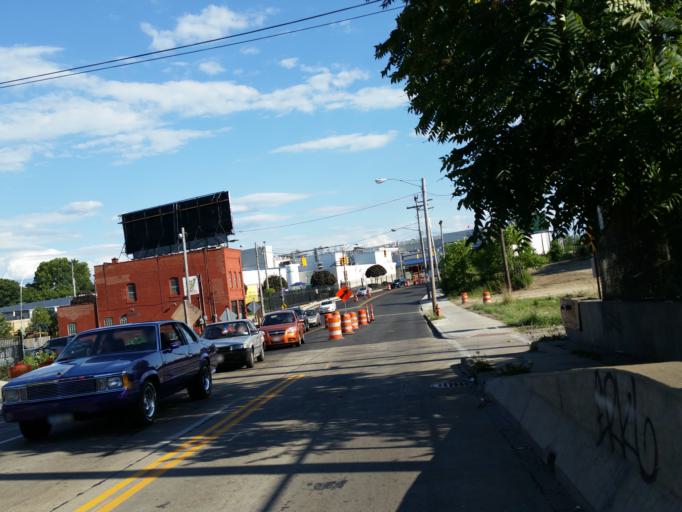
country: US
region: Ohio
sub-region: Cuyahoga County
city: Cleveland
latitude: 41.4782
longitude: -81.6996
